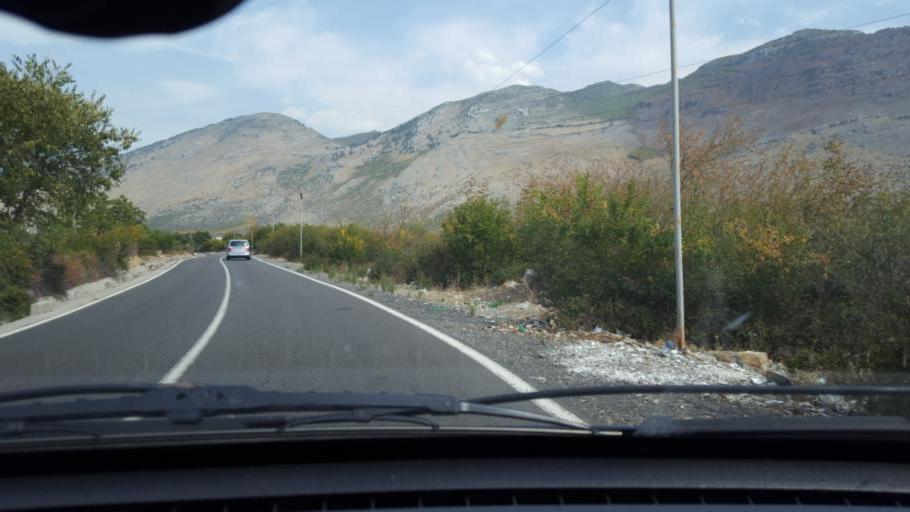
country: AL
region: Shkoder
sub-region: Rrethi i Malesia e Madhe
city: Hot
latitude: 42.3389
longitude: 19.4359
